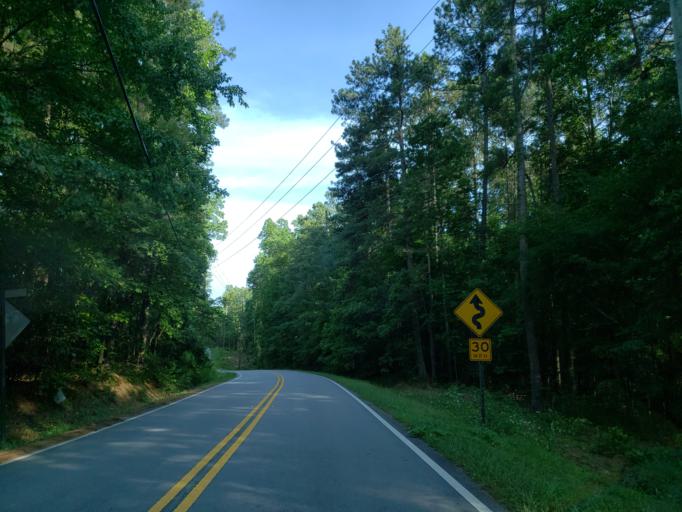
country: US
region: Georgia
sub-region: Paulding County
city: Hiram
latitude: 33.9193
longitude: -84.7224
